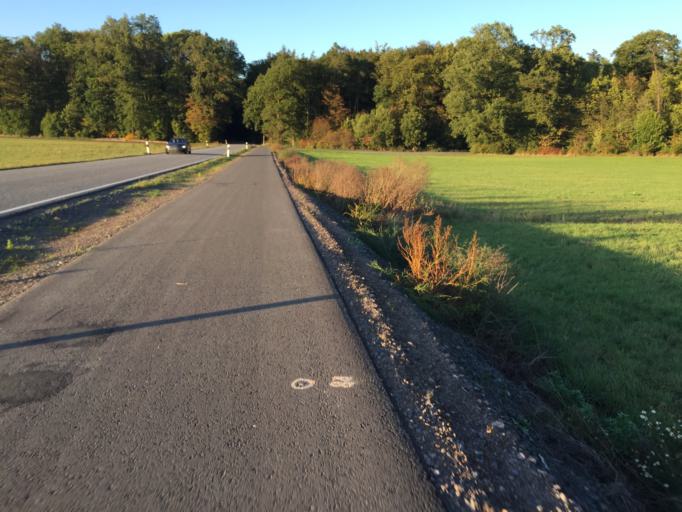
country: DE
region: Hesse
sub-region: Regierungsbezirk Giessen
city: Lich
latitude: 50.5134
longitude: 8.7599
